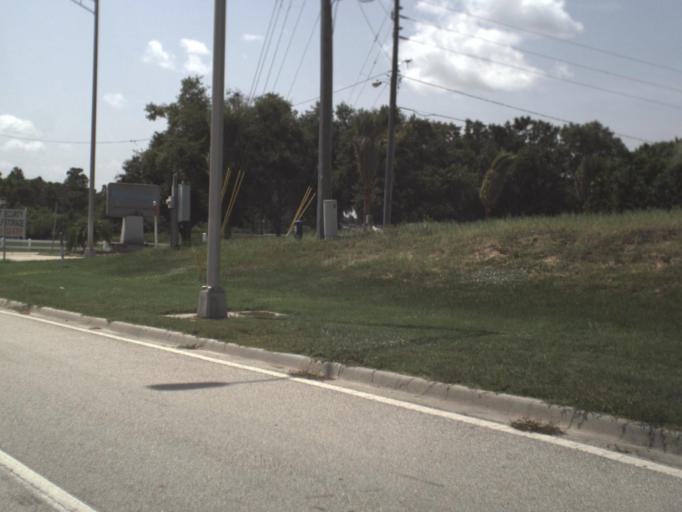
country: US
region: Florida
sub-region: Highlands County
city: Avon Park
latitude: 27.5704
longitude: -81.5145
